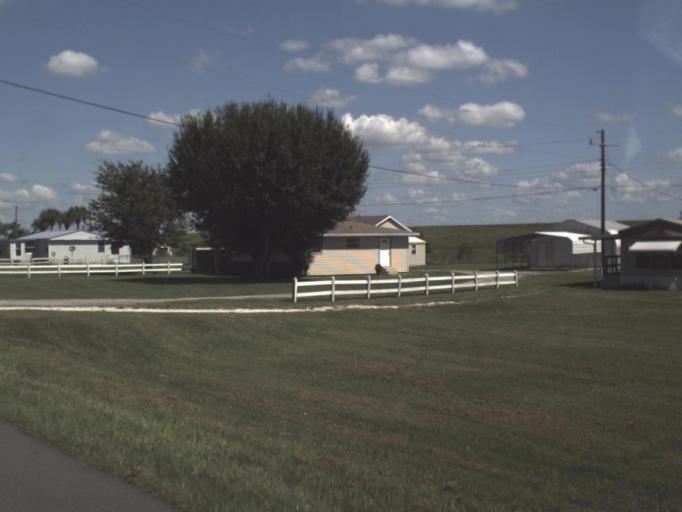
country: US
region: Florida
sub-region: Glades County
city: Buckhead Ridge
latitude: 27.1577
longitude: -80.8647
